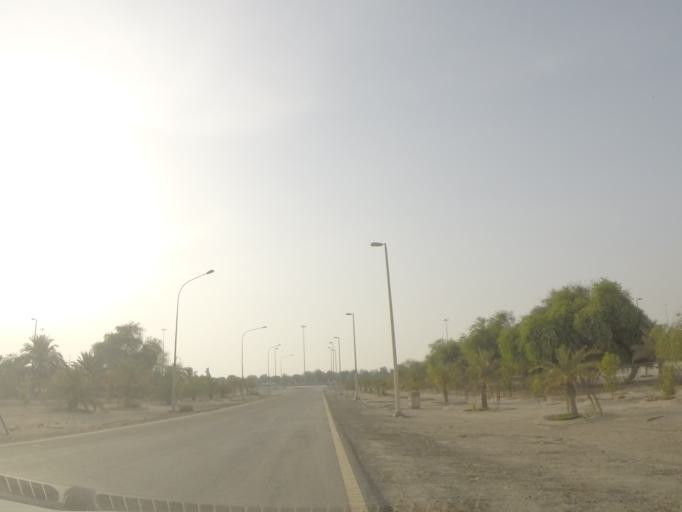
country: AE
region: Abu Dhabi
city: Abu Dhabi
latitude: 24.7037
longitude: 54.7905
